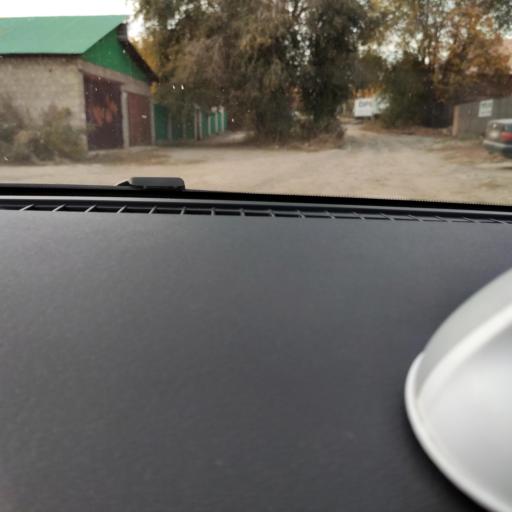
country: RU
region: Samara
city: Samara
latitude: 53.1757
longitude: 50.1730
